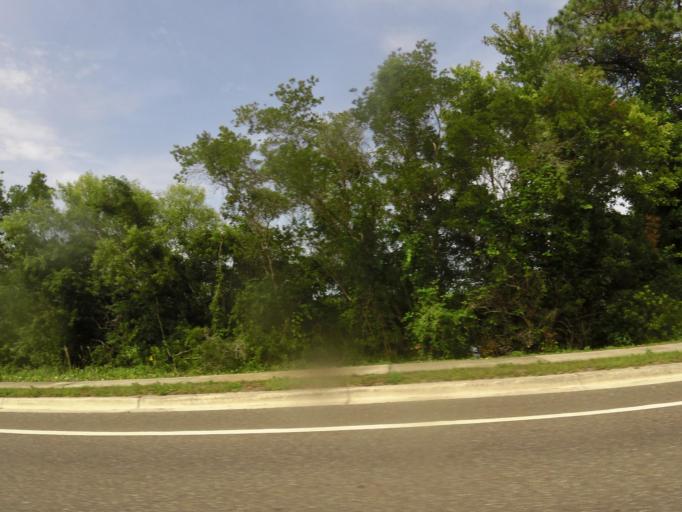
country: US
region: Florida
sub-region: Saint Johns County
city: Saint Augustine
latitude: 29.9001
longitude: -81.3601
